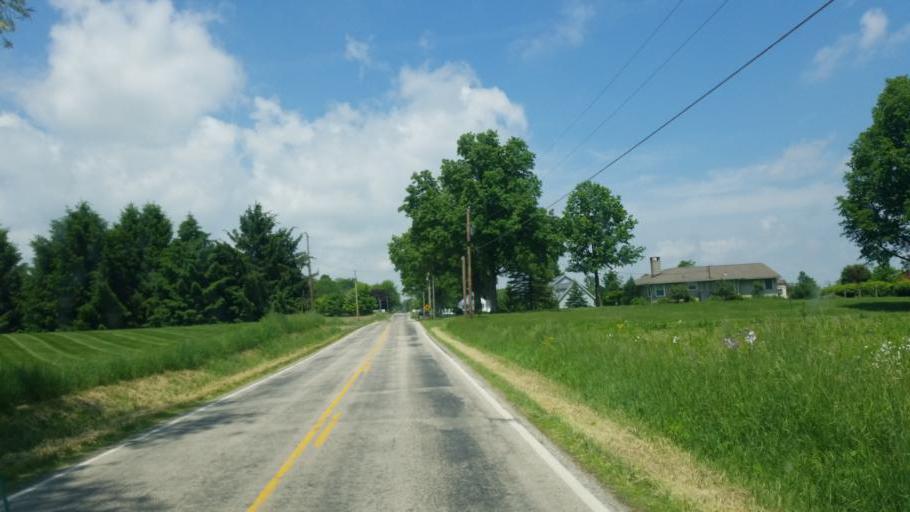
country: US
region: Ohio
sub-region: Ashland County
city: Ashland
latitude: 40.8265
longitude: -82.2717
